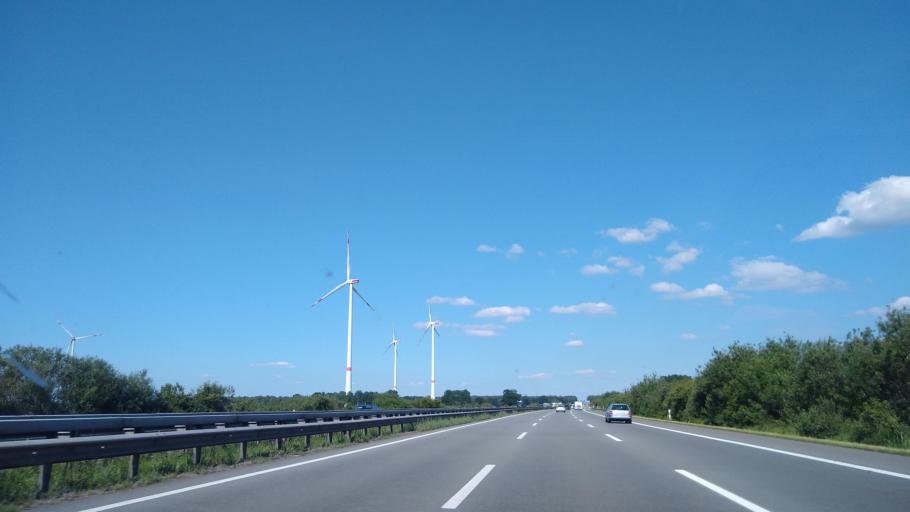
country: DE
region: Lower Saxony
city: Halvesbostel
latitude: 53.3272
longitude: 9.6010
